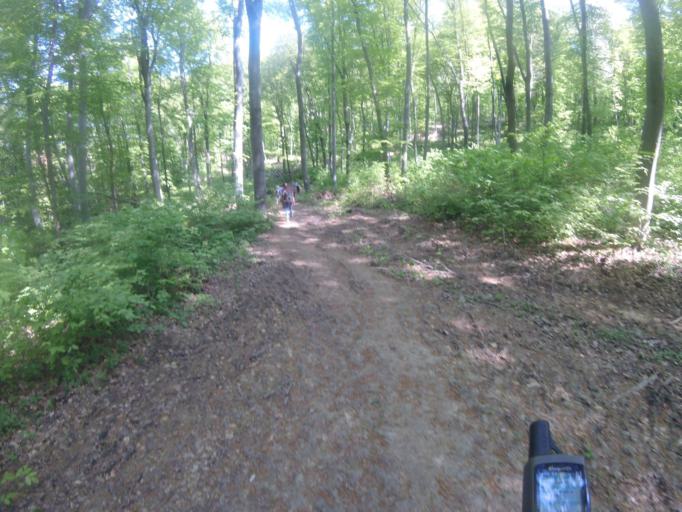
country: HU
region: Komarom-Esztergom
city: Piliscsev
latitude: 47.7071
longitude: 18.8395
